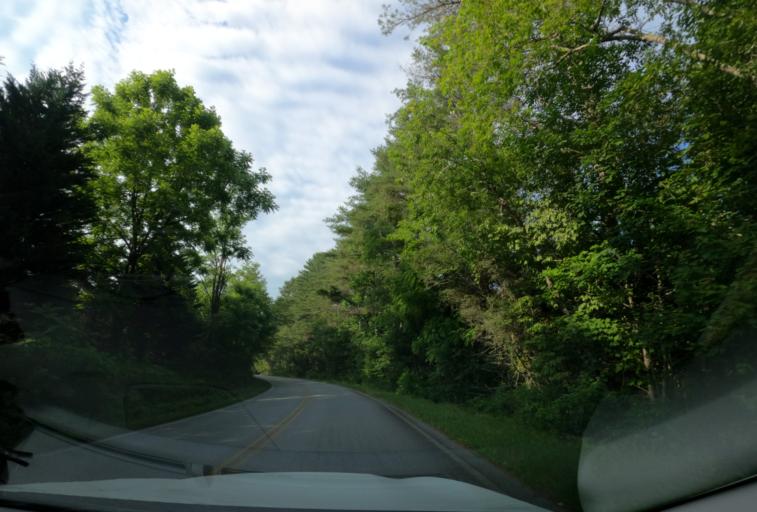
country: US
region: North Carolina
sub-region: Transylvania County
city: Brevard
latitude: 35.2083
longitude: -82.8591
